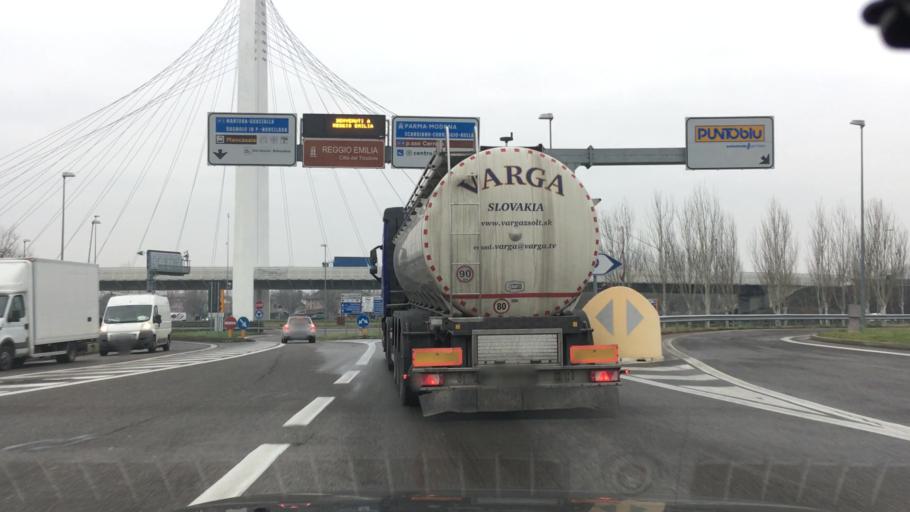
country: IT
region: Emilia-Romagna
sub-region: Provincia di Reggio Emilia
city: Reggio nell'Emilia
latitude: 44.7246
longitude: 10.6314
